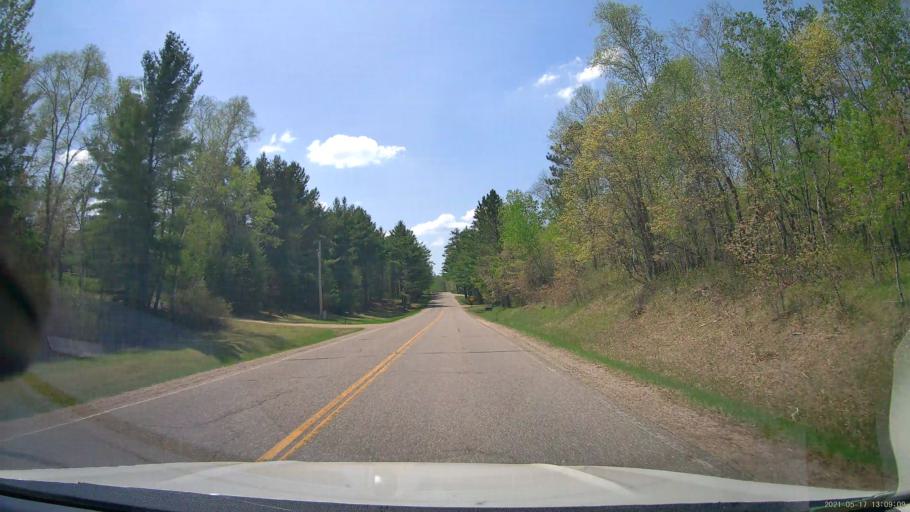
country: US
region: Minnesota
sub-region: Hubbard County
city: Park Rapids
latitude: 47.0298
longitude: -94.9256
